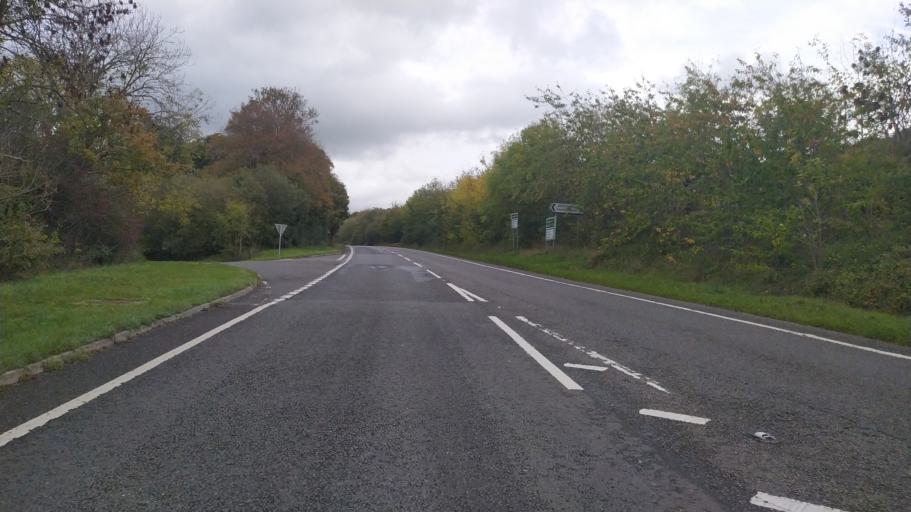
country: GB
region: England
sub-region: Dorset
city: Lyme Regis
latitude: 50.7405
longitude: -2.8844
